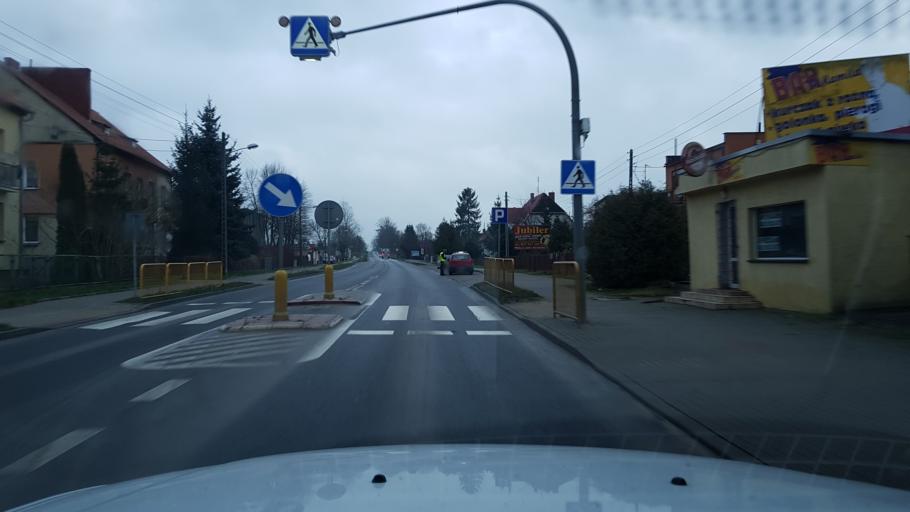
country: PL
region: West Pomeranian Voivodeship
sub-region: Powiat gryficki
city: Gryfice
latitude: 53.9075
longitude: 15.2007
